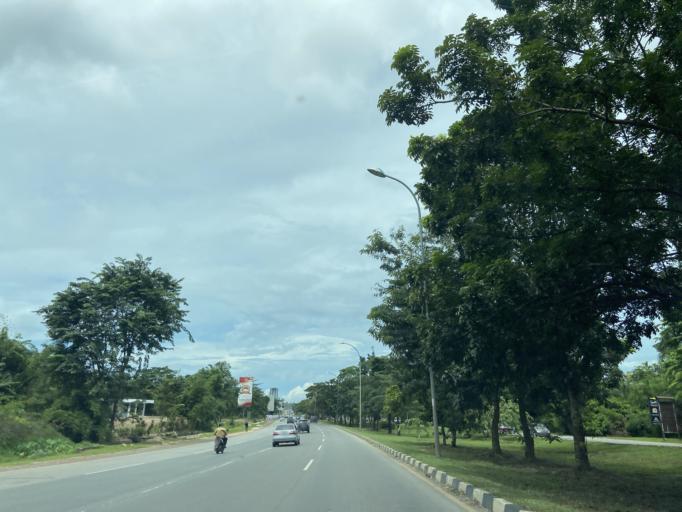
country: SG
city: Singapore
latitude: 1.1040
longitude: 104.0348
